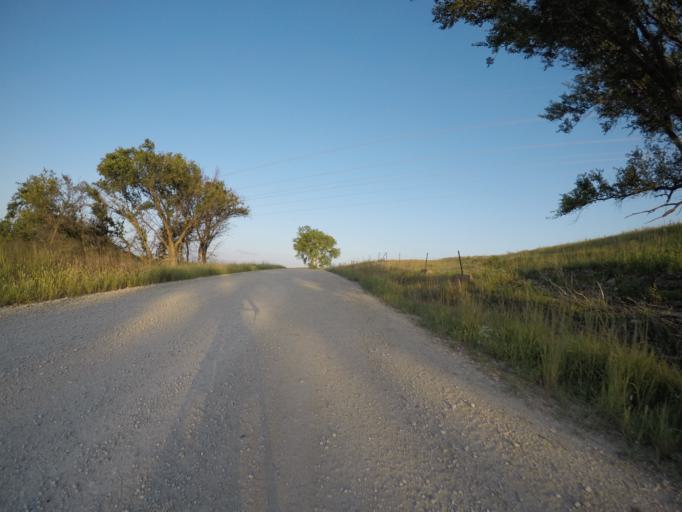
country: US
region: Kansas
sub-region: Riley County
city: Ogden
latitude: 39.0087
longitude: -96.6403
